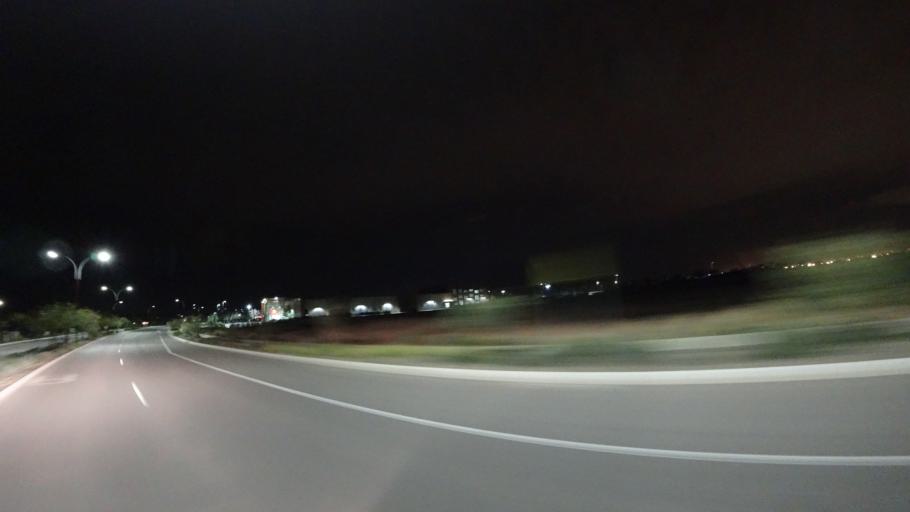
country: US
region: Arizona
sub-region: Maricopa County
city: Queen Creek
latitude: 33.3262
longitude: -111.6158
